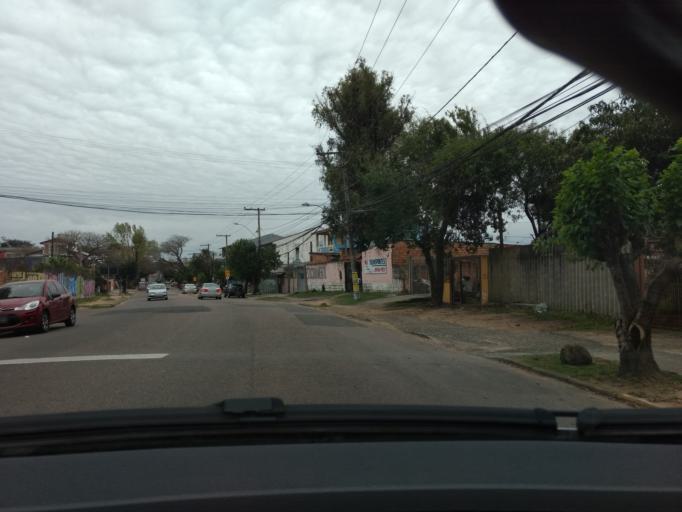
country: BR
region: Rio Grande do Sul
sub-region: Cachoeirinha
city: Cachoeirinha
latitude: -30.0269
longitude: -51.1316
